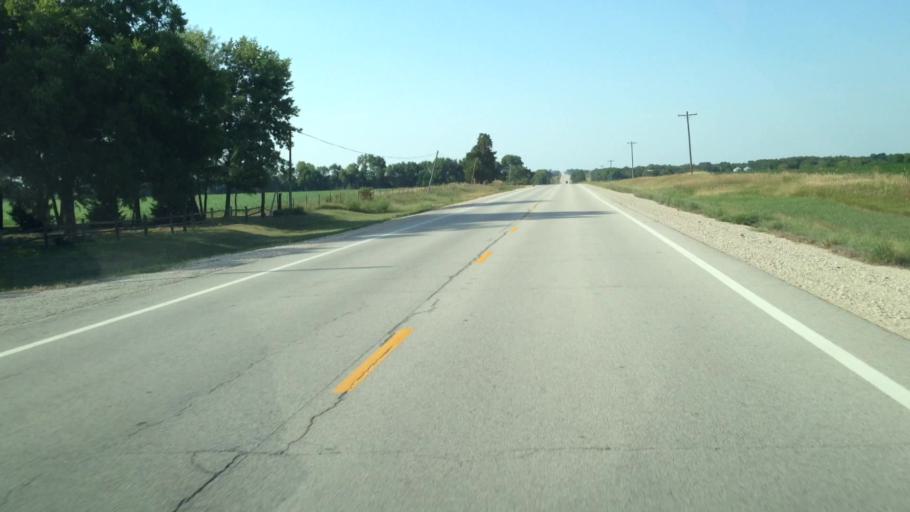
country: US
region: Kansas
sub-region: Anderson County
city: Garnett
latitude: 38.0993
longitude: -95.2430
